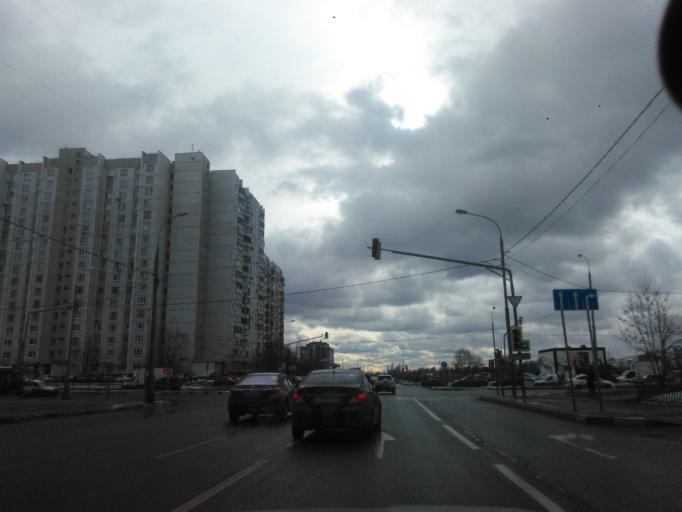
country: RU
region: Moskovskaya
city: Pavshino
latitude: 55.8428
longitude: 37.3531
